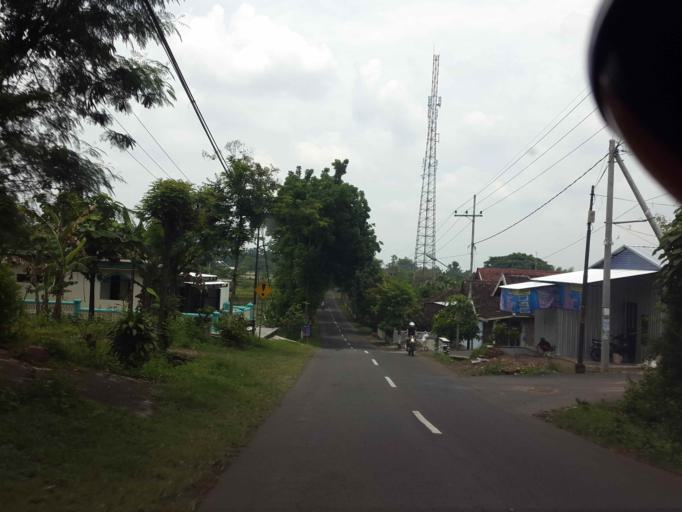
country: ID
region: East Java
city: Madiun
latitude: -7.6659
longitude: 111.3401
